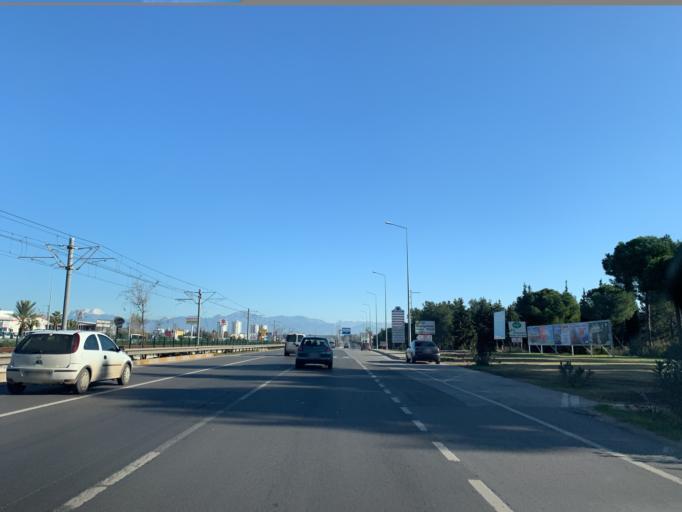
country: TR
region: Antalya
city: Aksu
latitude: 36.9329
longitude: 30.8100
